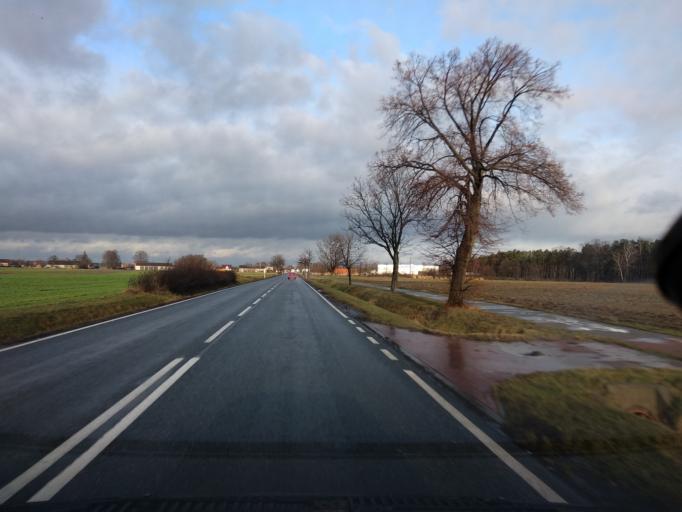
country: PL
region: Greater Poland Voivodeship
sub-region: Powiat koninski
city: Rychwal
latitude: 52.0896
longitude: 18.1643
